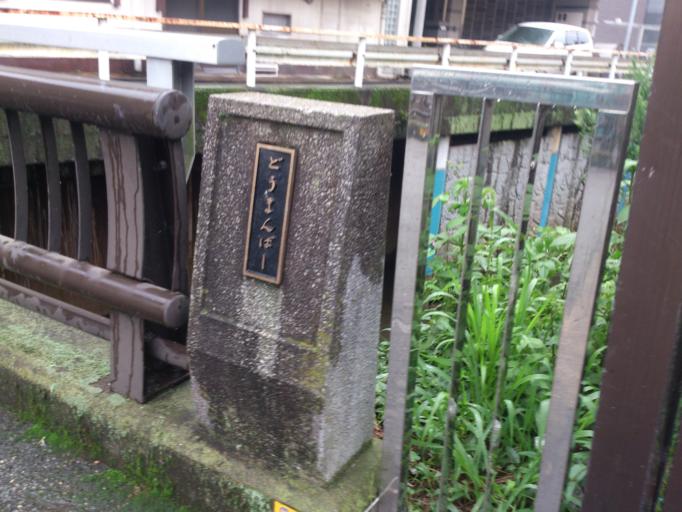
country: JP
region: Chiba
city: Chiba
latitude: 35.6157
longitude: 140.1221
